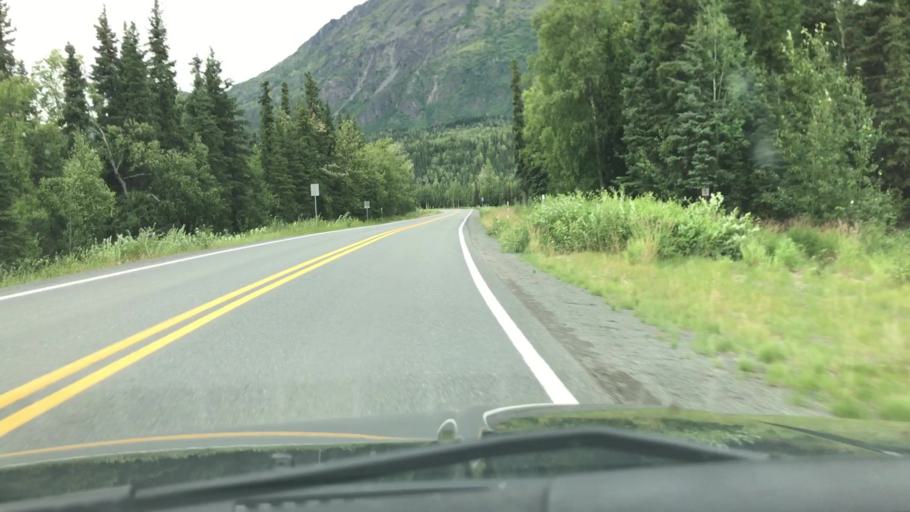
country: US
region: Alaska
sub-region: Kenai Peninsula Borough
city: Seward
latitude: 60.4844
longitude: -149.9600
